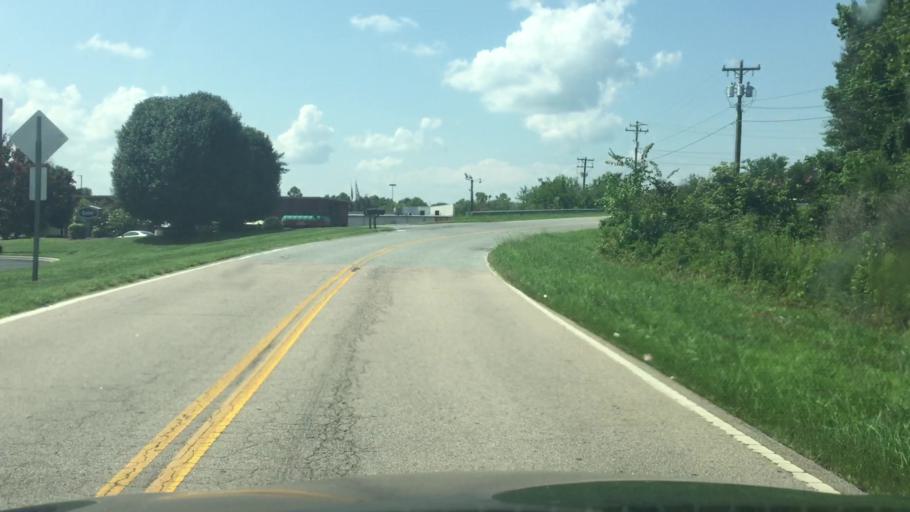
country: US
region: North Carolina
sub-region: Rowan County
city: Salisbury
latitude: 35.6424
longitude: -80.4833
